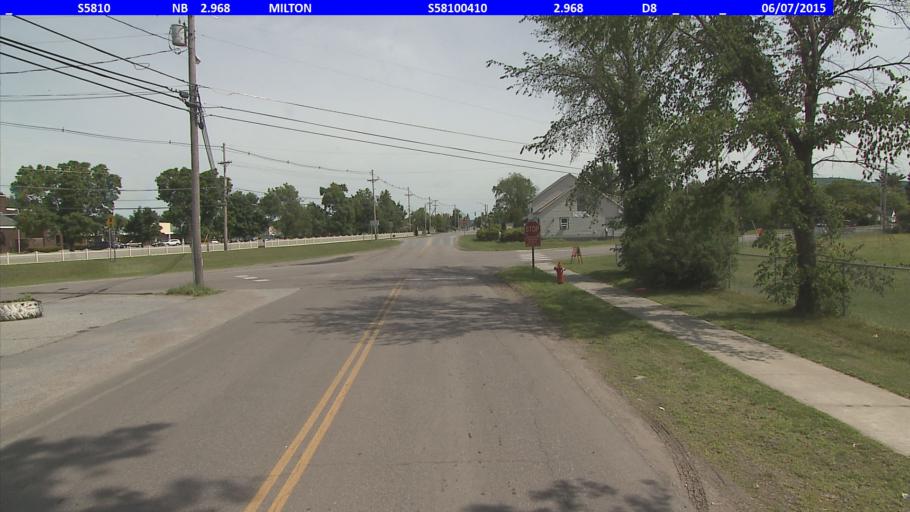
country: US
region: Vermont
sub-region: Chittenden County
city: Milton
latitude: 44.6234
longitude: -73.1185
